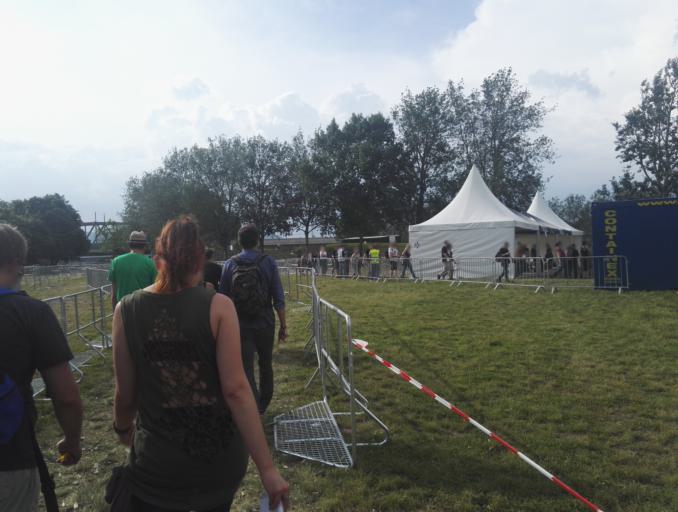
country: AT
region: Vienna
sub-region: Wien Stadt
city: Vienna
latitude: 48.2428
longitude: 16.3925
